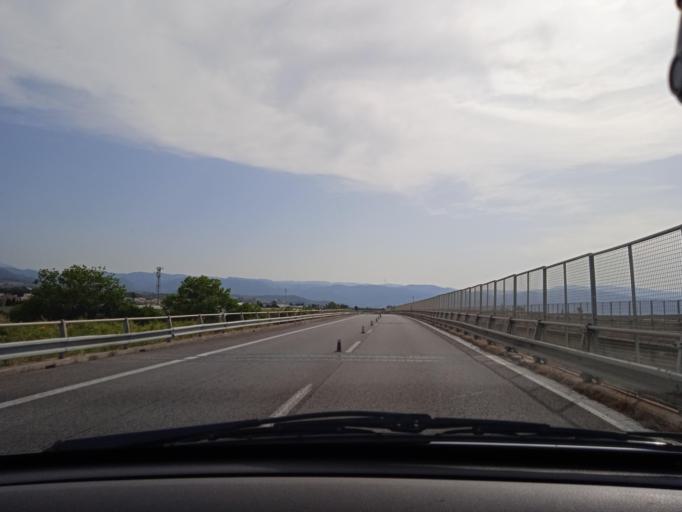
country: IT
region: Sicily
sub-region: Messina
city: Terme
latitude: 38.1492
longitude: 15.1738
